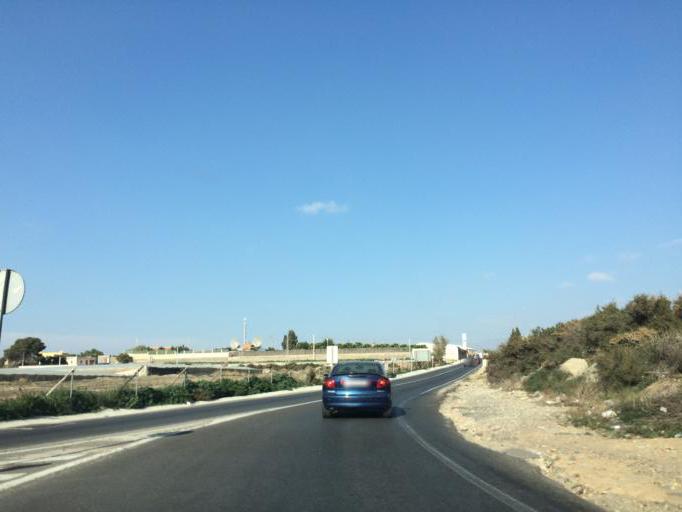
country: ES
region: Andalusia
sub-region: Provincia de Almeria
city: Huercal de Almeria
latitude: 36.8540
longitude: -2.4203
